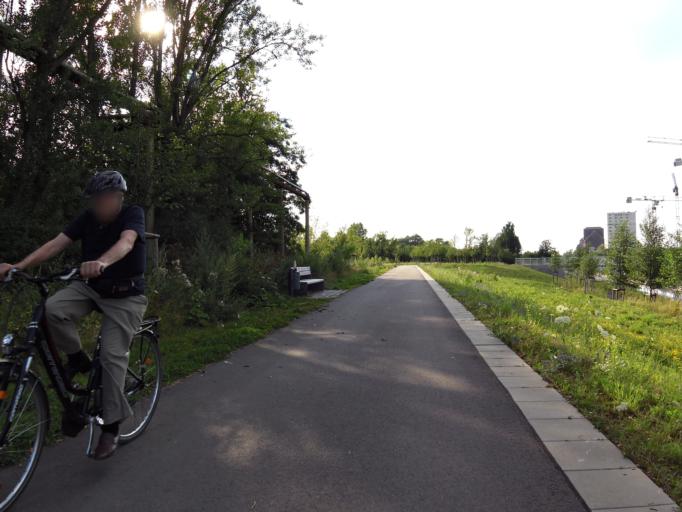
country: DE
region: Saxony
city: Leipzig
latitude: 51.3296
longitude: 12.3059
